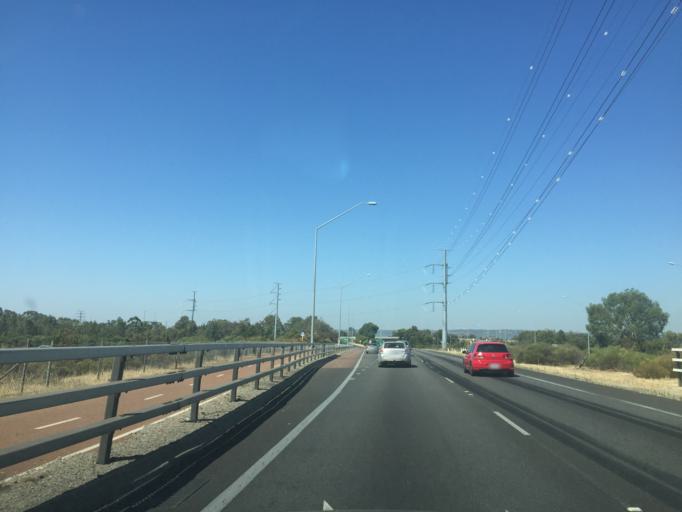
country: AU
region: Western Australia
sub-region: Gosnells
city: Kenwick
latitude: -32.0397
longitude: 115.9554
